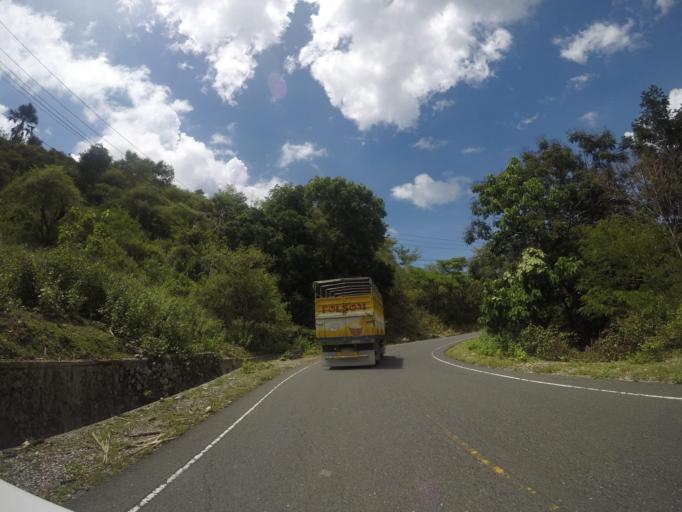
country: TL
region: Bobonaro
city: Maliana
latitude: -8.9513
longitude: 125.1076
